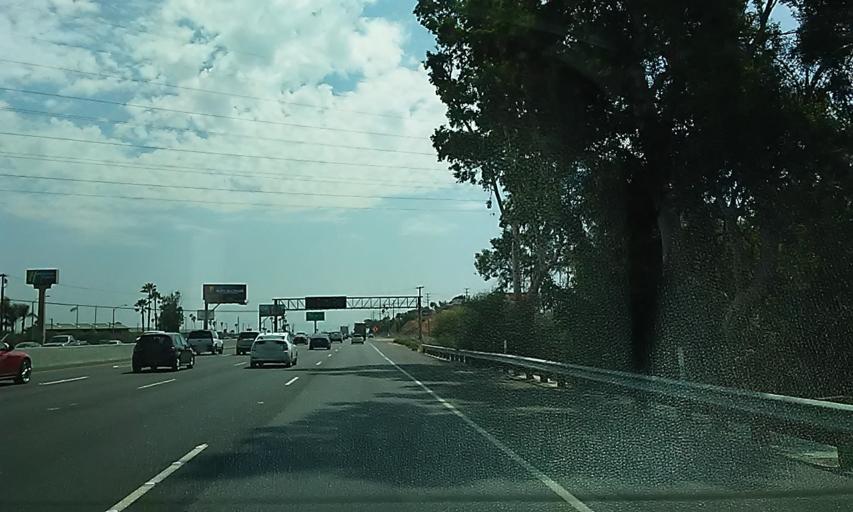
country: US
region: California
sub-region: Riverside County
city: Highgrove
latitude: 34.0229
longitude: -117.3367
